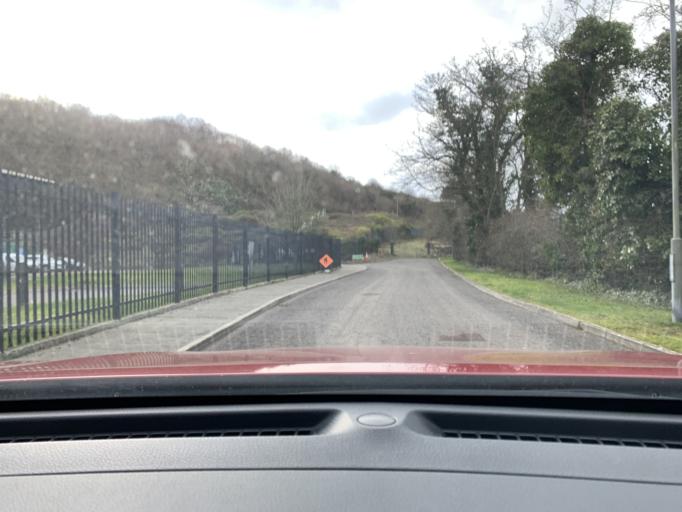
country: IE
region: Connaught
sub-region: Sligo
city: Sligo
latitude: 54.2556
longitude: -8.4552
